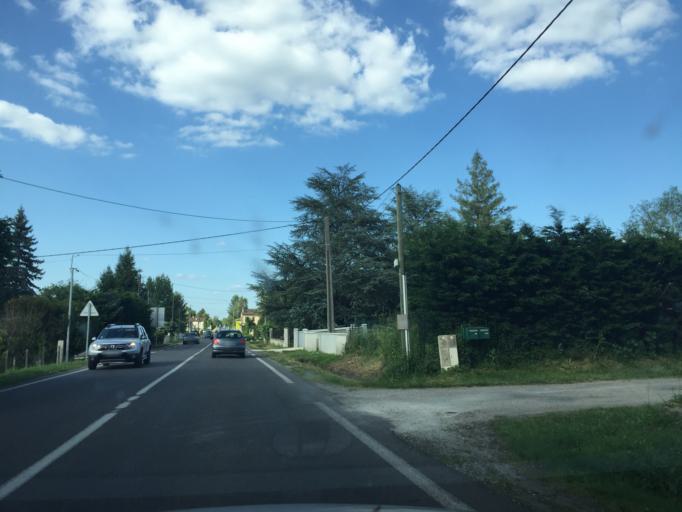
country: FR
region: Aquitaine
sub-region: Departement de la Gironde
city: Saint-Denis-de-Pile
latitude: 44.9824
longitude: -0.2072
